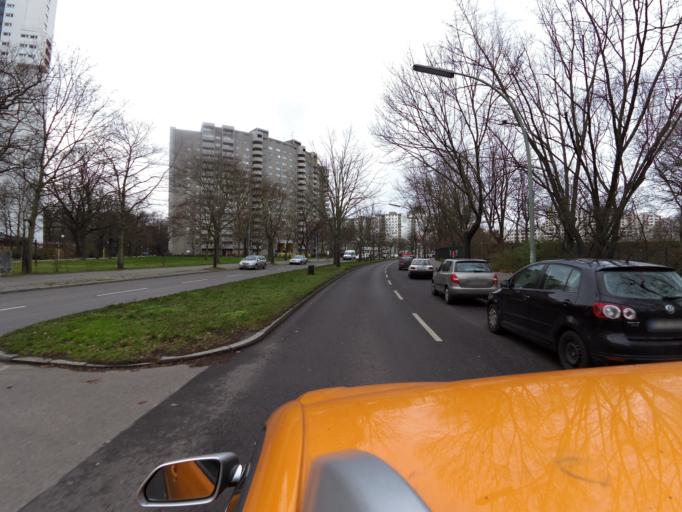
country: DE
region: Berlin
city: Gropiusstadt
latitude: 52.4261
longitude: 13.4712
